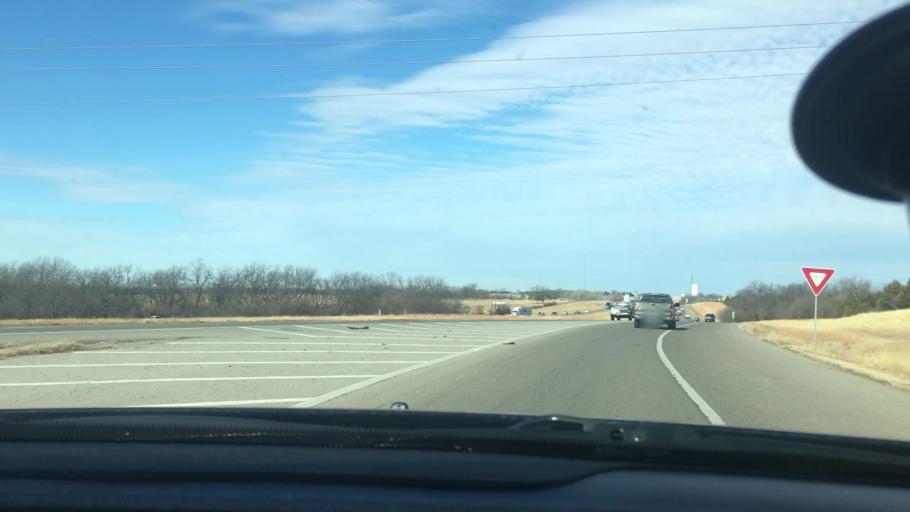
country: US
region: Oklahoma
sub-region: McClain County
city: Purcell
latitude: 35.0478
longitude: -97.3779
